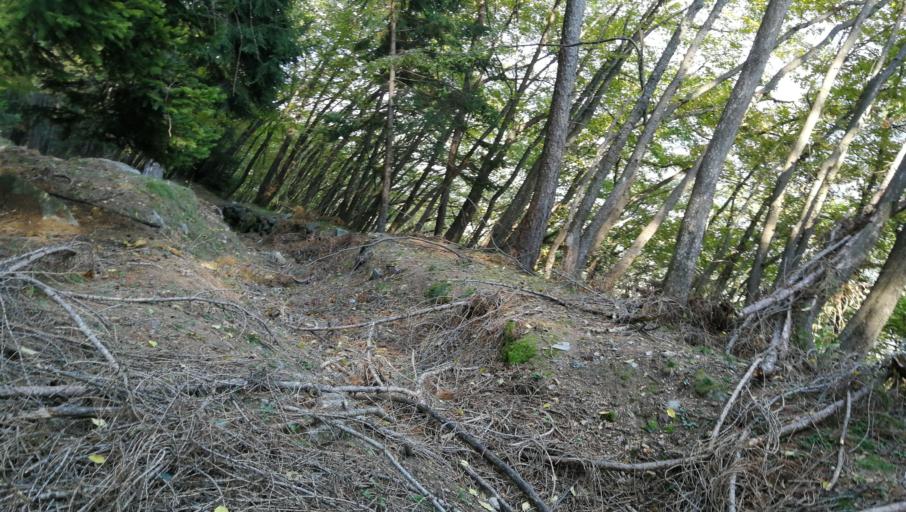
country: IT
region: Trentino-Alto Adige
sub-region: Provincia di Trento
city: Cimego
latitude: 45.9210
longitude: 10.6154
